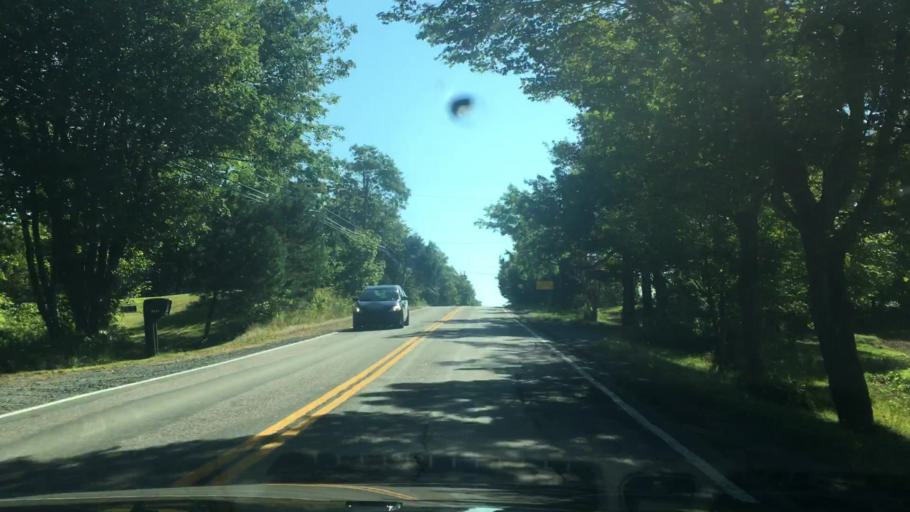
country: CA
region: Nova Scotia
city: Cole Harbour
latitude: 44.7780
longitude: -63.0600
